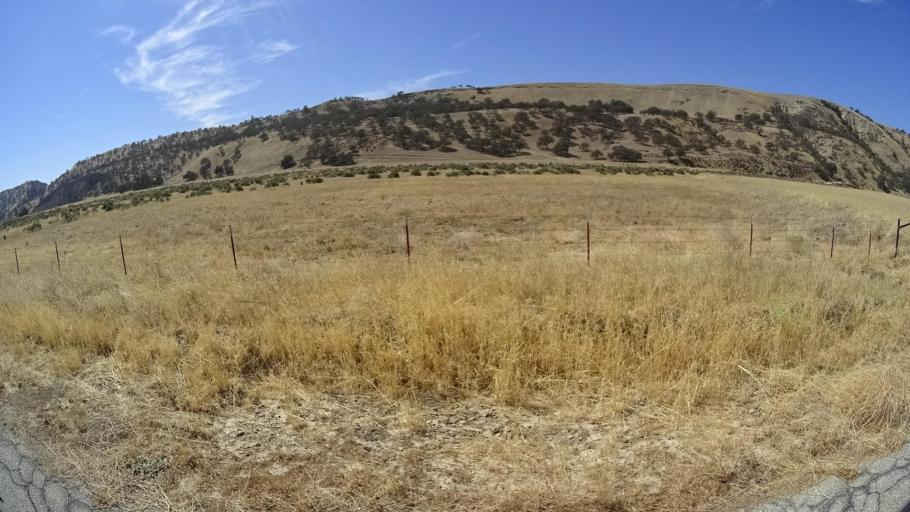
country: US
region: California
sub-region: San Luis Obispo County
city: San Miguel
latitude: 35.8686
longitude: -120.7019
